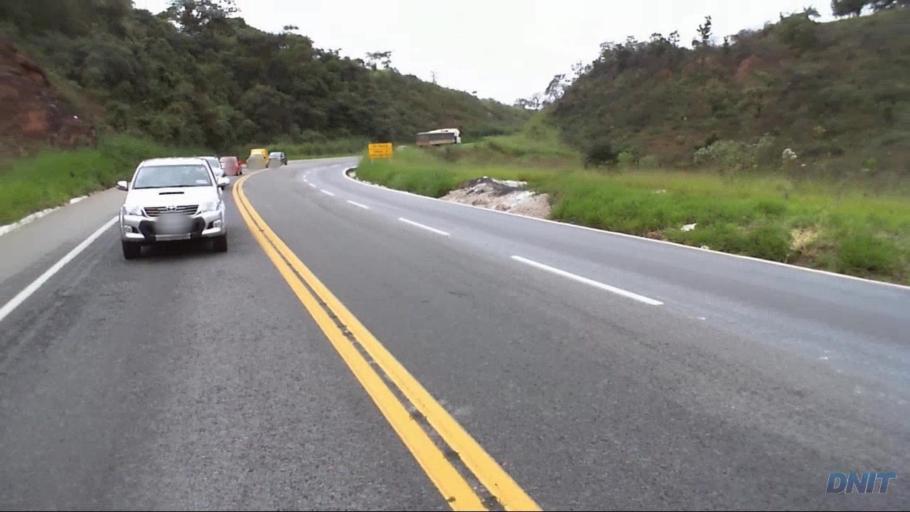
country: BR
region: Minas Gerais
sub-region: Joao Monlevade
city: Joao Monlevade
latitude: -19.8475
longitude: -43.3051
